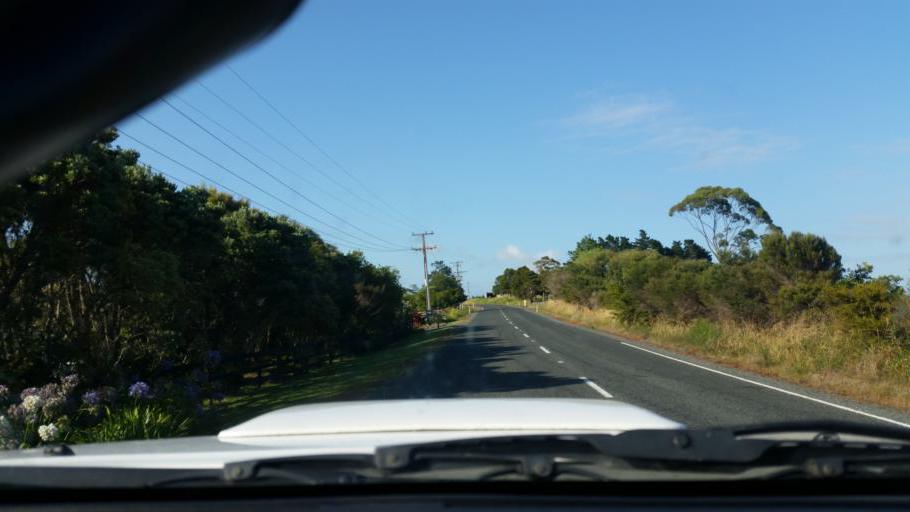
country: NZ
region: Northland
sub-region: Whangarei
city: Ruakaka
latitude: -36.1245
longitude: 174.2323
